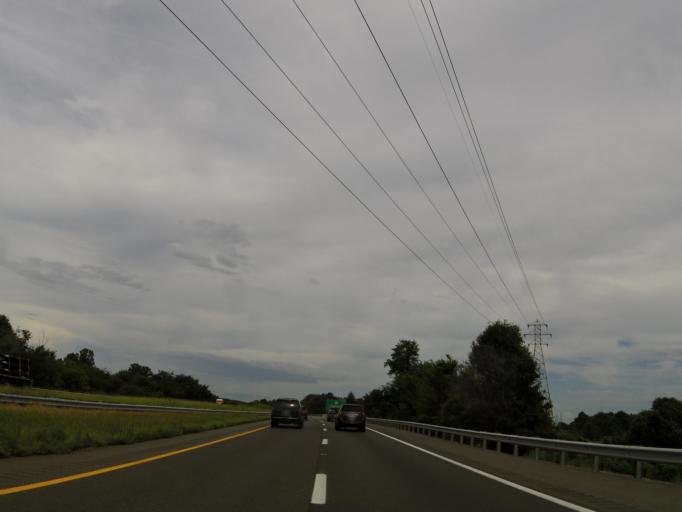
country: US
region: Kentucky
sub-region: Marshall County
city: Calvert City
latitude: 37.0167
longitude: -88.2976
